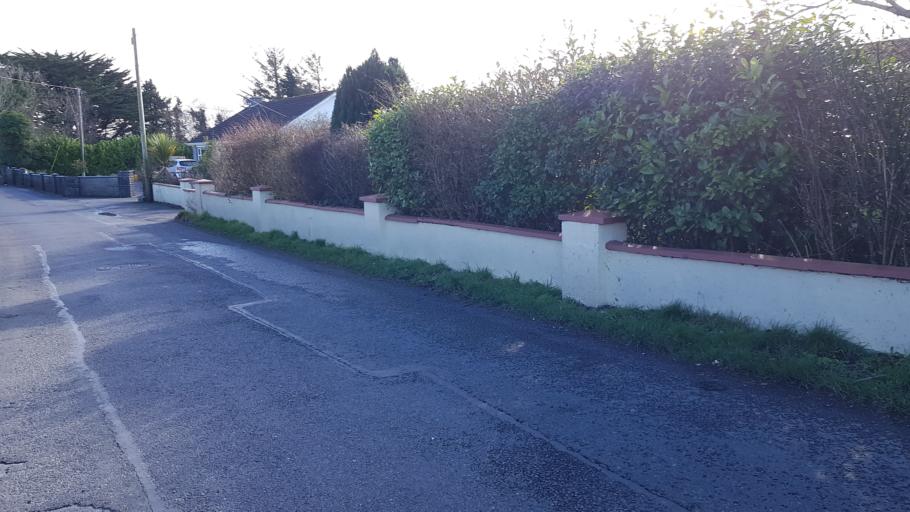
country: IE
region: Connaught
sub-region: County Galway
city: Gaillimh
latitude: 53.3014
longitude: -9.0193
